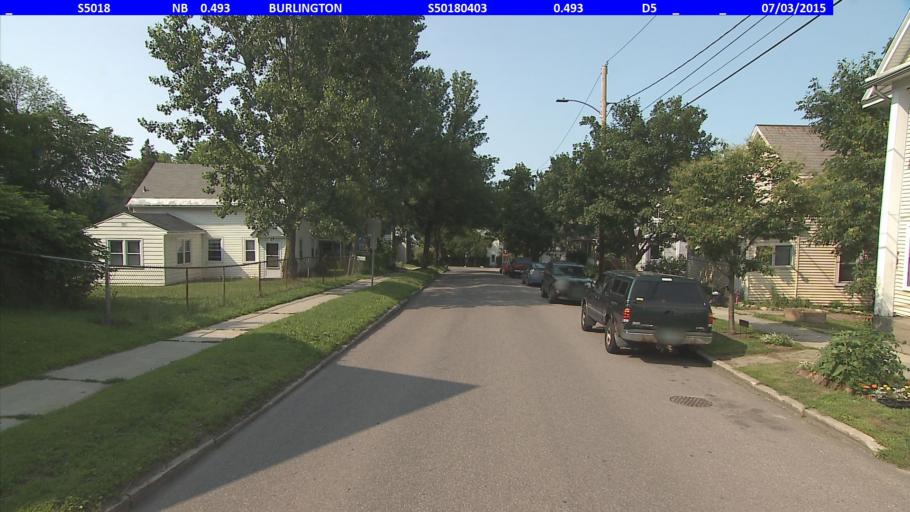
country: US
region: Vermont
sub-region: Chittenden County
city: Winooski
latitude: 44.4867
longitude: -73.1837
